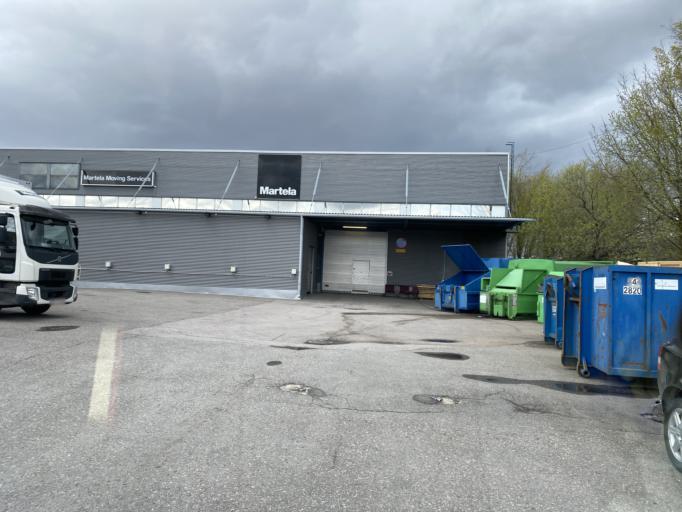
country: FI
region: Pirkanmaa
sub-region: Tampere
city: Tampere
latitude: 61.4797
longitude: 23.7868
